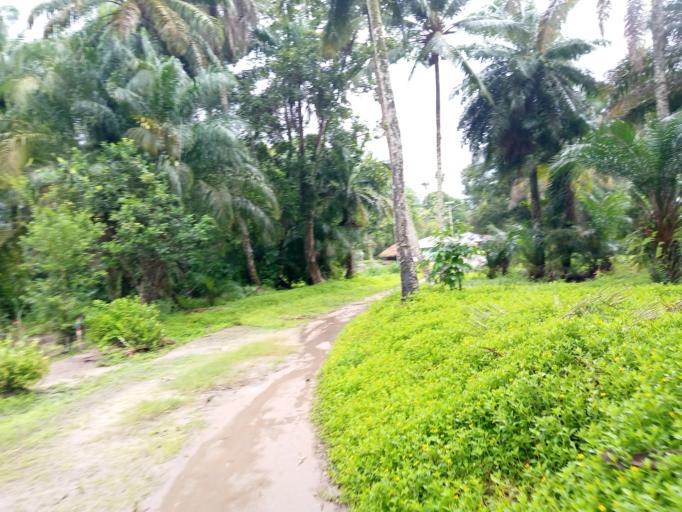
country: SL
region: Southern Province
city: Bonthe
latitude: 7.5339
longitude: -12.5095
